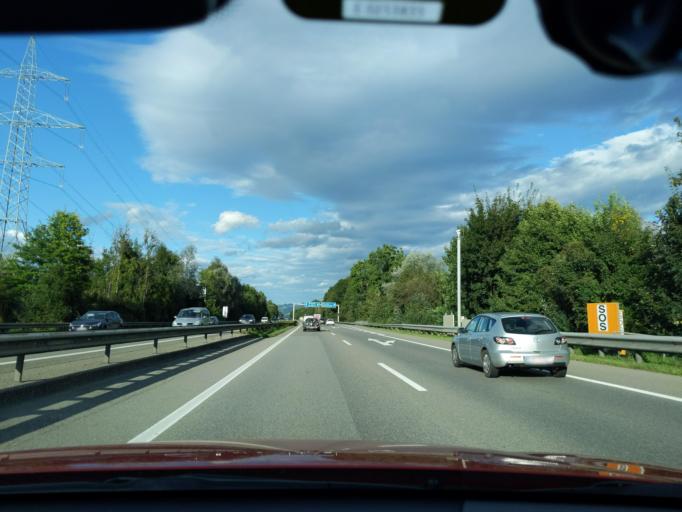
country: CH
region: Saint Gallen
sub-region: Wahlkreis Rheintal
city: Diepoldsau
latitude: 47.3713
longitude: 9.6653
